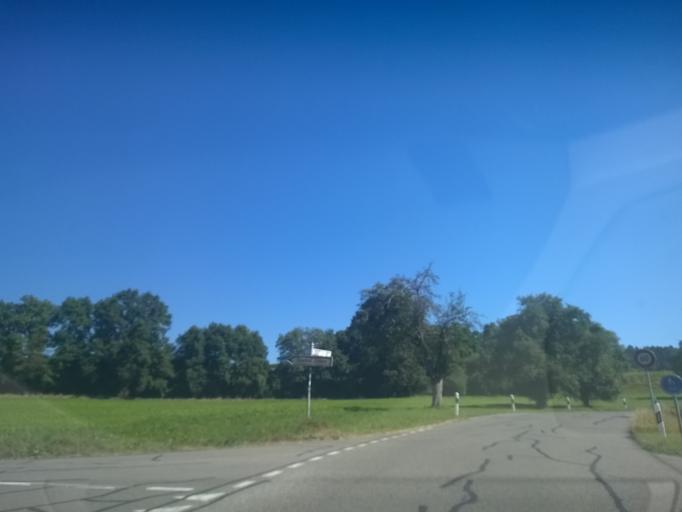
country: CH
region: Zurich
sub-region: Bezirk Buelach
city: Kloten / Geissberg
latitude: 47.4592
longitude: 8.5929
